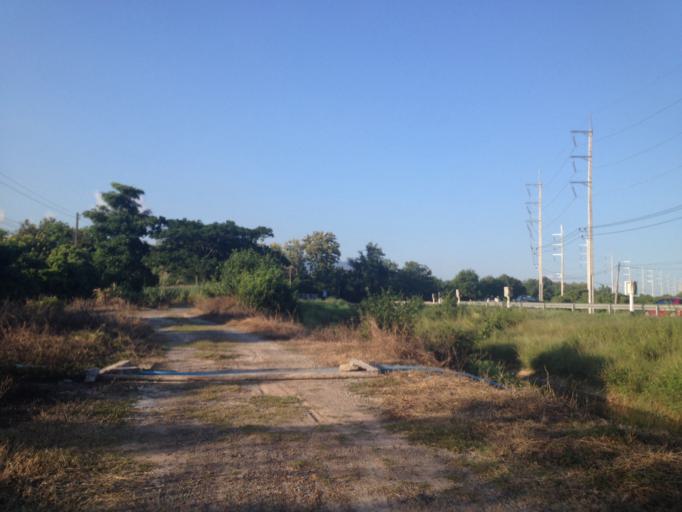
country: TH
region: Chiang Mai
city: Hang Dong
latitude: 18.6908
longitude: 98.8961
